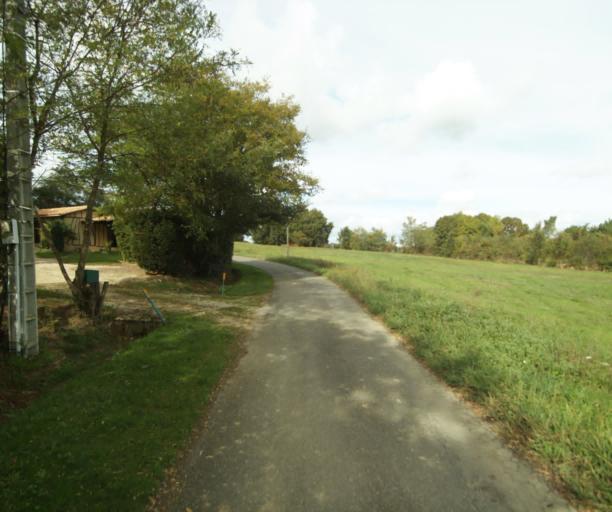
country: FR
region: Midi-Pyrenees
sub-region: Departement du Gers
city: Eauze
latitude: 43.8552
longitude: 0.0740
